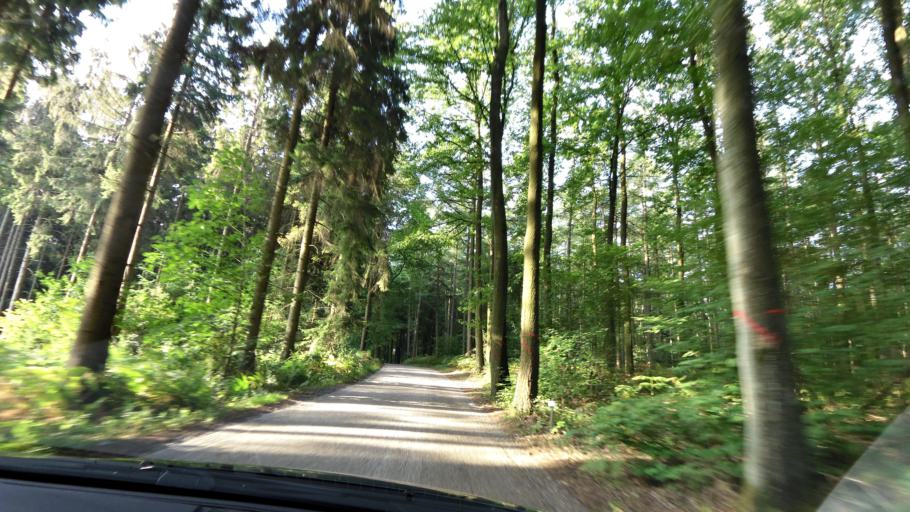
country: BE
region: Wallonia
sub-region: Province de Liege
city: Plombieres
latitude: 50.7757
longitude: 5.9637
